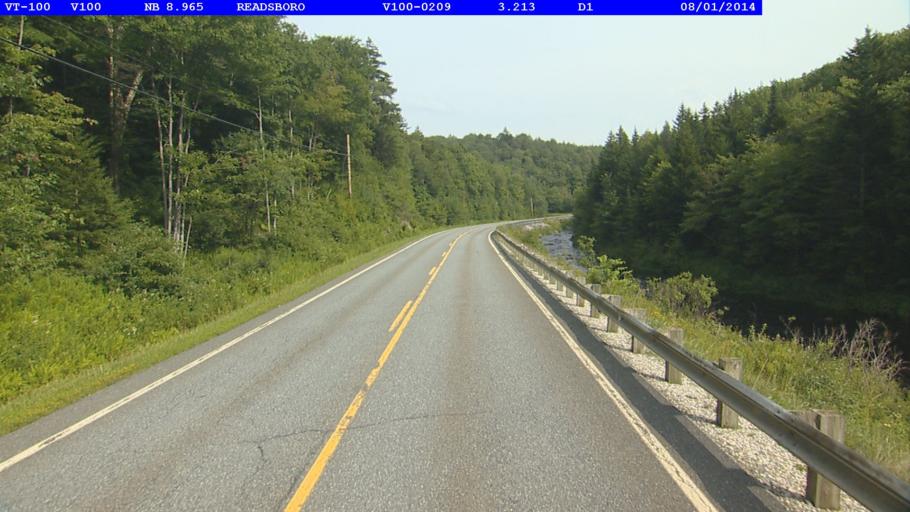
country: US
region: Massachusetts
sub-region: Berkshire County
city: North Adams
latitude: 42.8174
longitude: -72.9753
